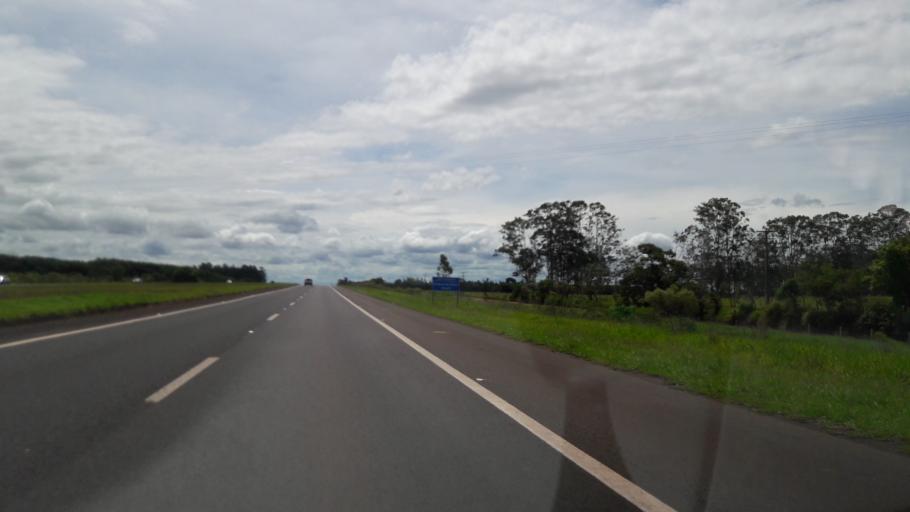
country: BR
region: Sao Paulo
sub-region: Avare
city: Avare
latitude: -22.9328
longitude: -48.9977
